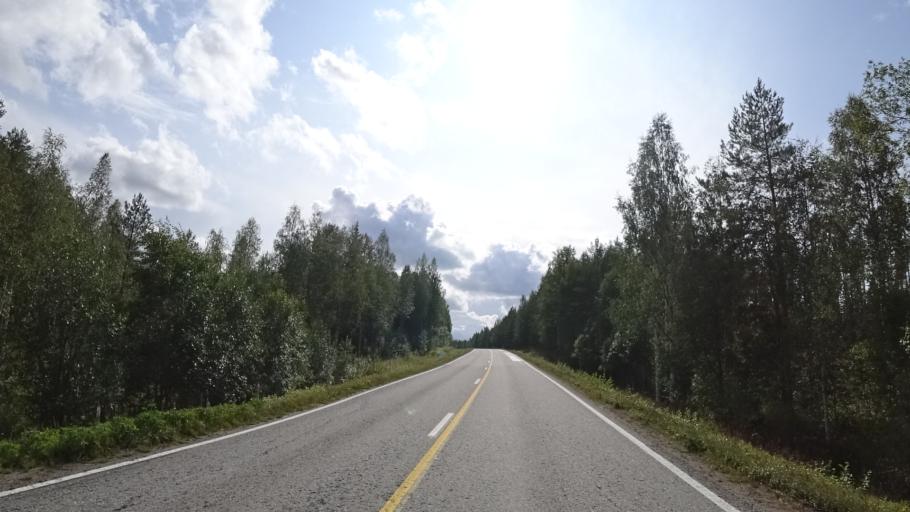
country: FI
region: North Karelia
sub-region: Joensuu
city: Ilomantsi
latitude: 62.6953
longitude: 30.9867
